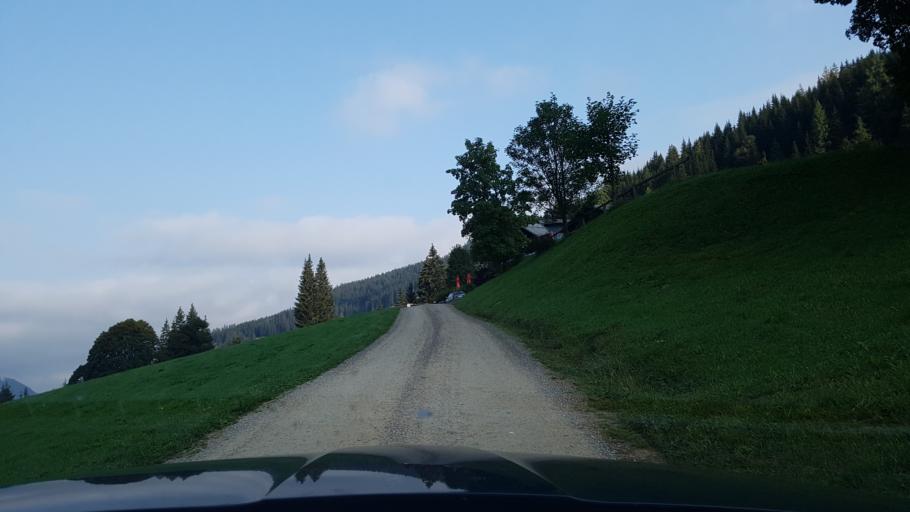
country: AT
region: Salzburg
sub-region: Politischer Bezirk Sankt Johann im Pongau
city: Kleinarl
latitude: 47.2725
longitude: 13.2528
